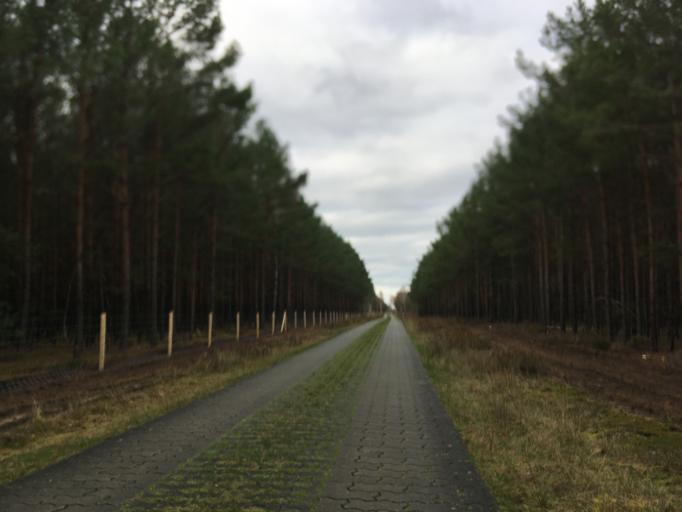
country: DE
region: Brandenburg
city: Tauer
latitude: 51.9973
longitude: 14.5108
